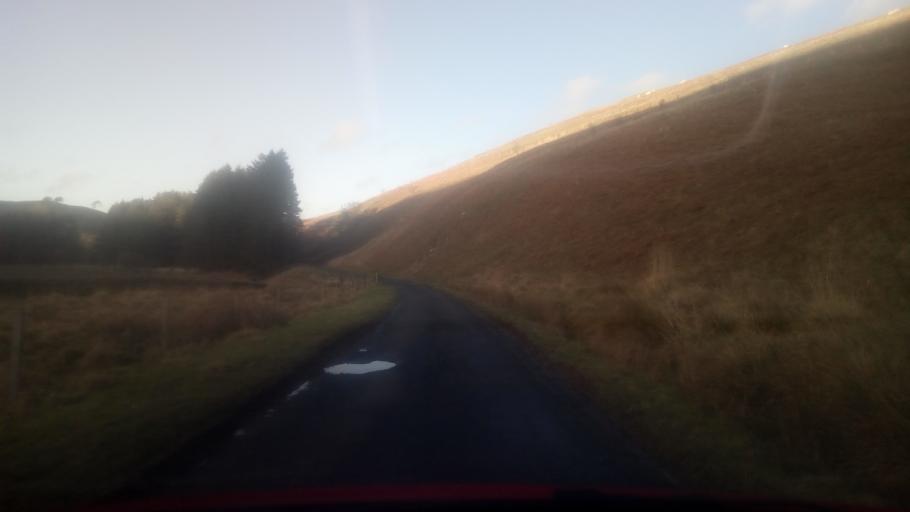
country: GB
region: Scotland
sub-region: The Scottish Borders
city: Kelso
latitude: 55.4447
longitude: -2.3629
